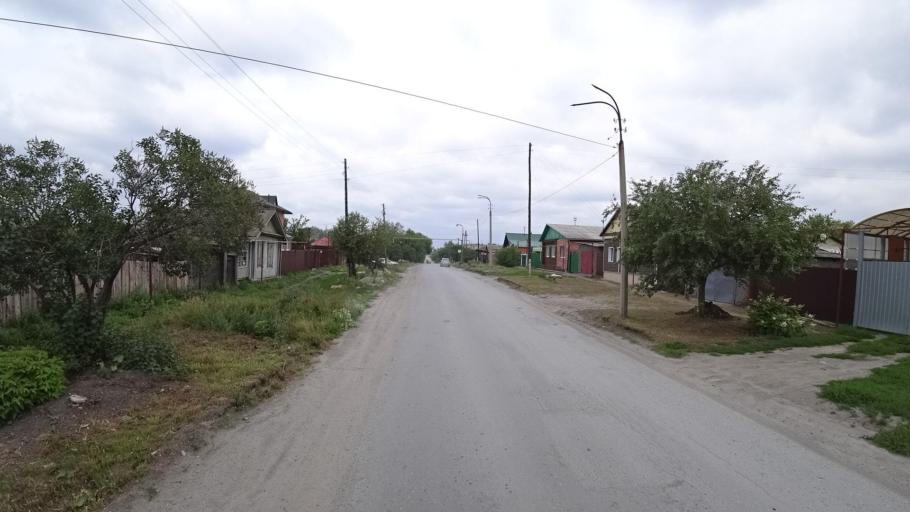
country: RU
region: Sverdlovsk
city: Kamyshlov
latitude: 56.8358
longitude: 62.7180
